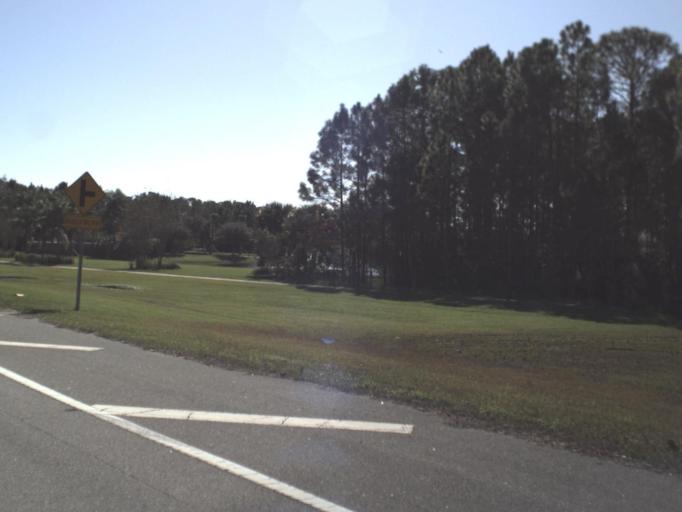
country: US
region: Florida
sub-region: Volusia County
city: Port Orange
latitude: 29.1141
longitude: -81.0443
